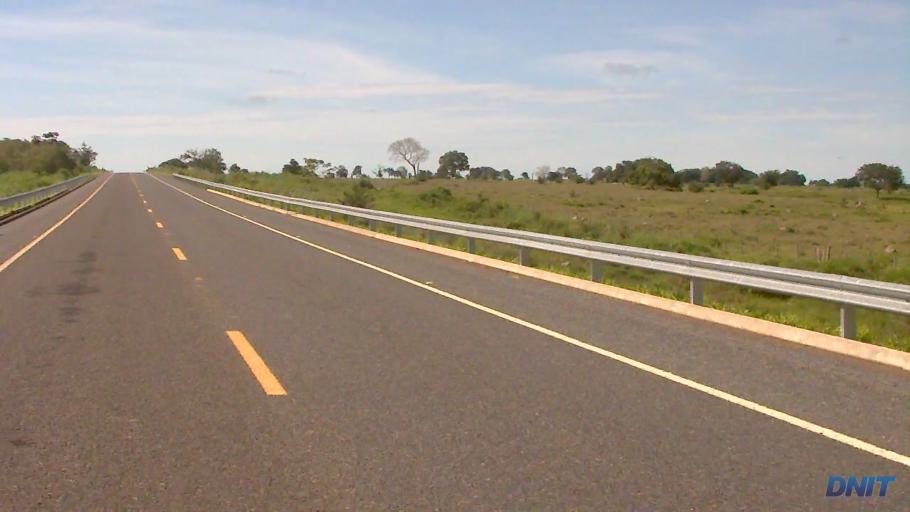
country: BR
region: Goias
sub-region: Sao Miguel Do Araguaia
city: Sao Miguel do Araguaia
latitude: -13.4526
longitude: -50.1201
